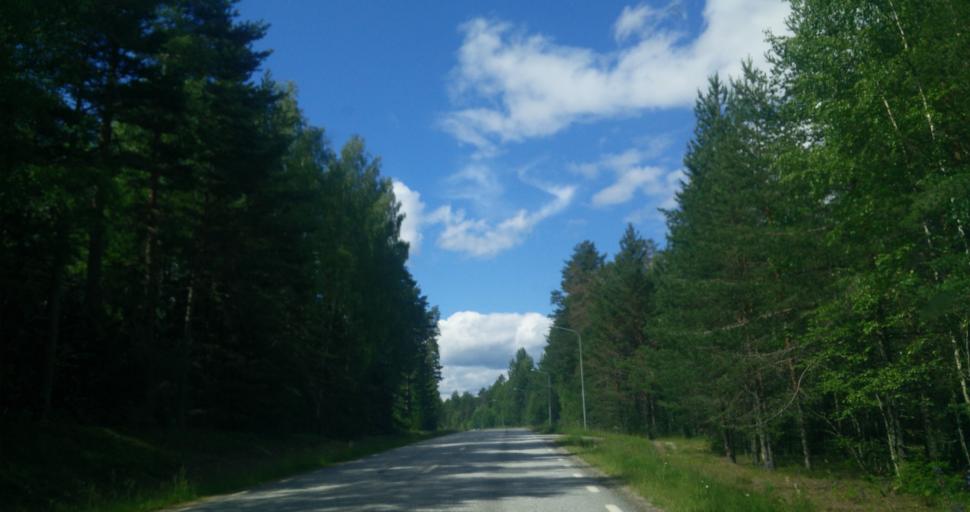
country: SE
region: Gaevleborg
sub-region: Nordanstigs Kommun
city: Bergsjoe
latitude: 62.0088
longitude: 16.9524
